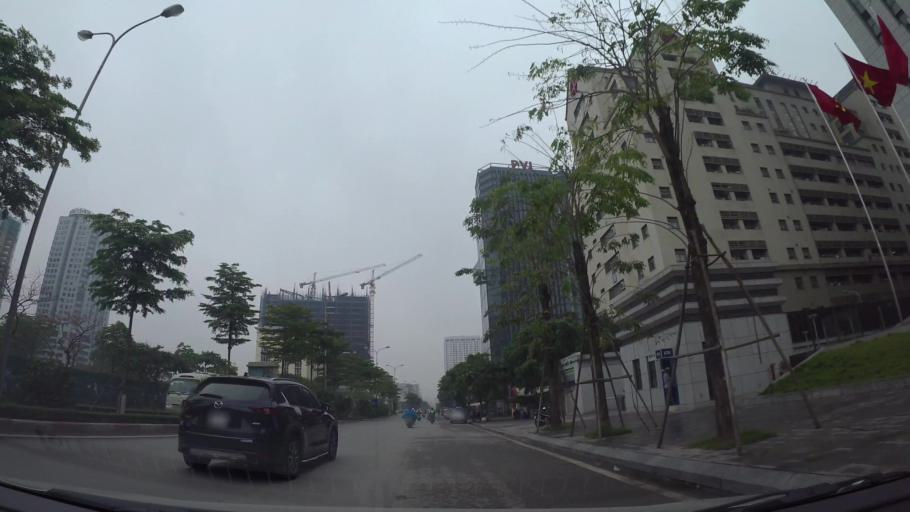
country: VN
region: Ha Noi
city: Cau Giay
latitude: 21.0255
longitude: 105.7886
